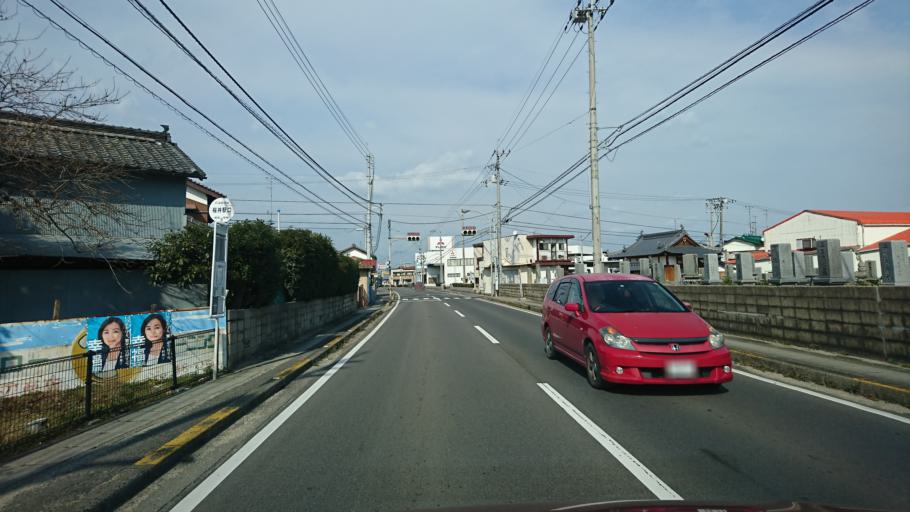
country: JP
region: Ehime
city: Saijo
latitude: 34.0124
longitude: 133.0388
